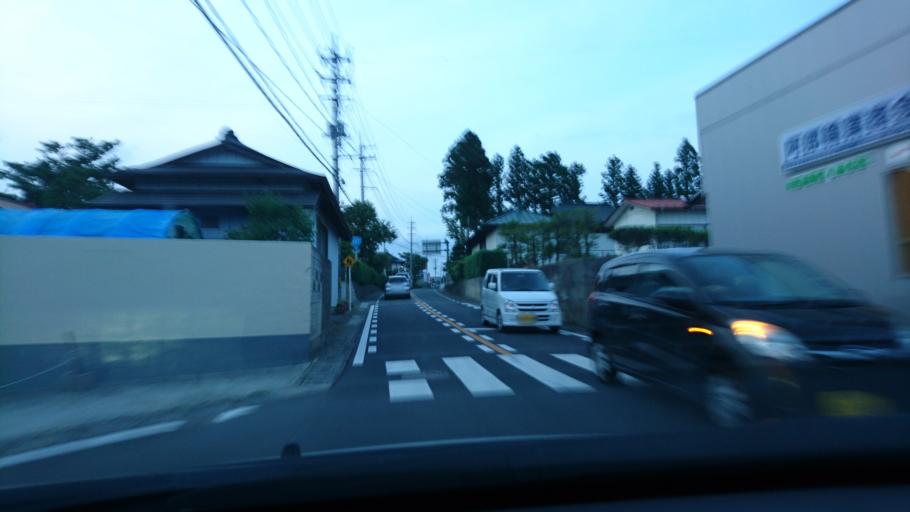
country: JP
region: Iwate
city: Ichinoseki
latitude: 38.8093
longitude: 140.9836
